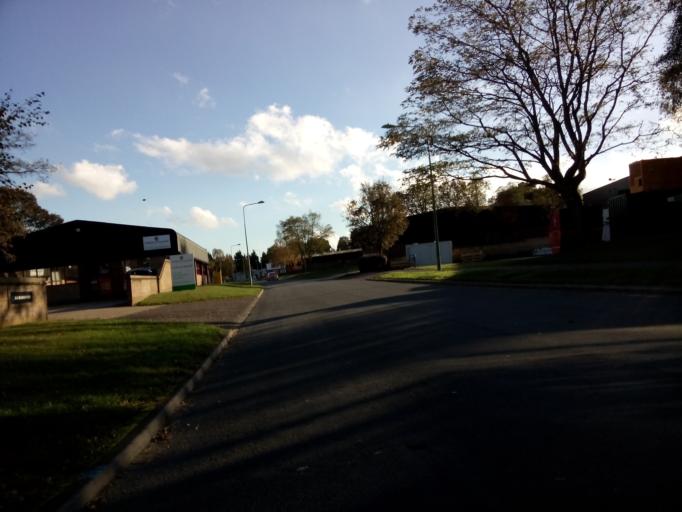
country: GB
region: England
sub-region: Suffolk
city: Kesgrave
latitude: 52.0640
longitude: 1.2805
